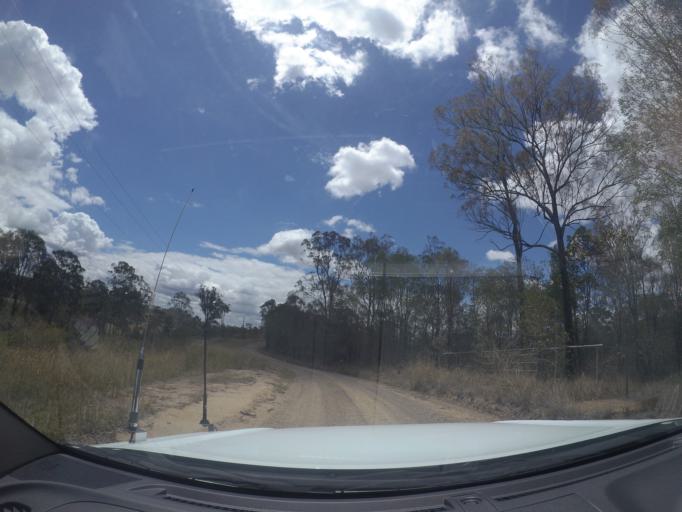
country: AU
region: Queensland
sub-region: Logan
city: Cedar Vale
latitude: -27.9134
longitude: 153.0537
